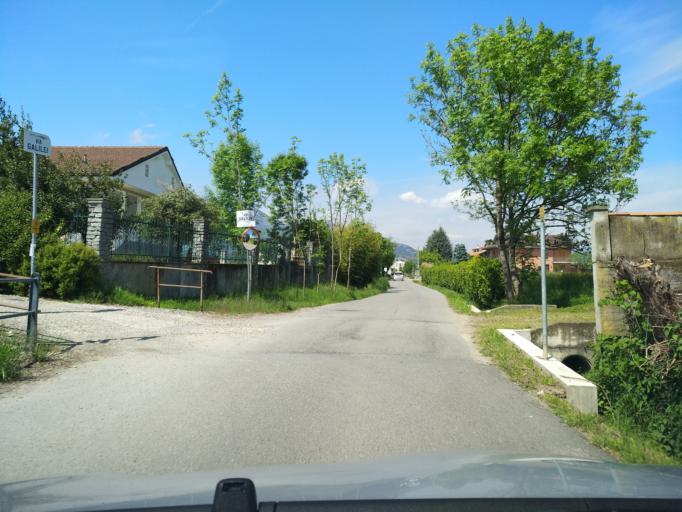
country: IT
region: Piedmont
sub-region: Provincia di Torino
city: Frossasco
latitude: 44.9041
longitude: 7.3556
